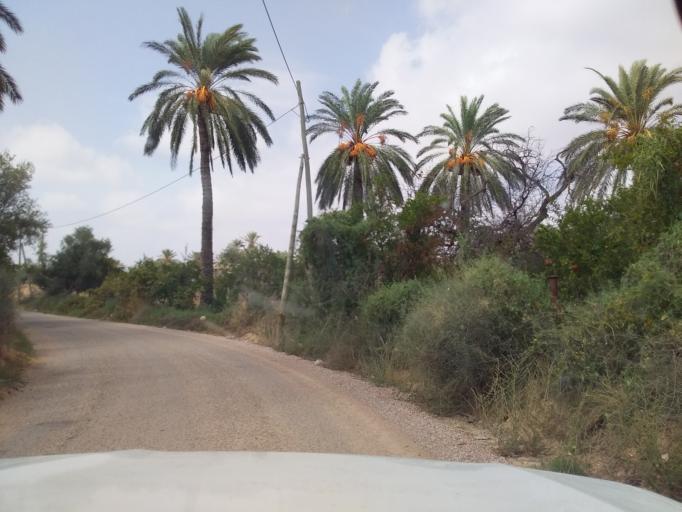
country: TN
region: Qabis
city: Gabes
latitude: 33.6259
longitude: 10.3103
